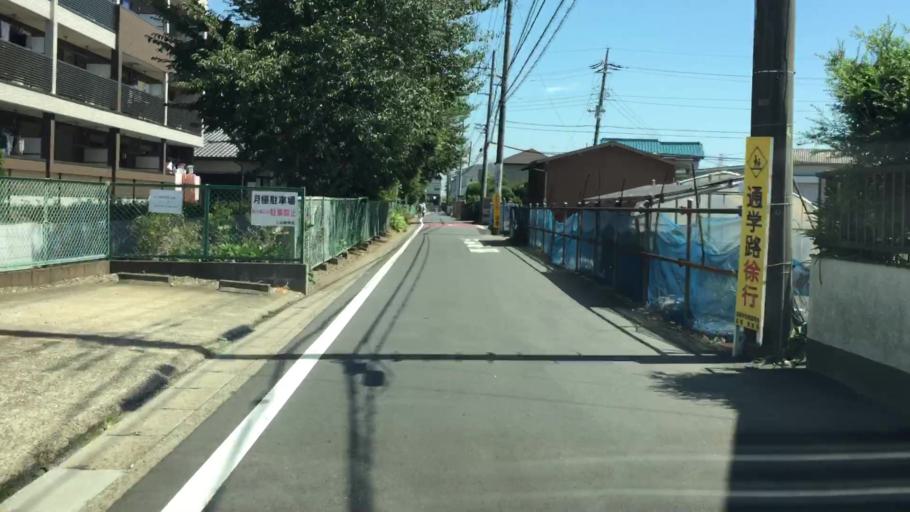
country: JP
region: Chiba
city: Funabashi
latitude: 35.7341
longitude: 139.9787
